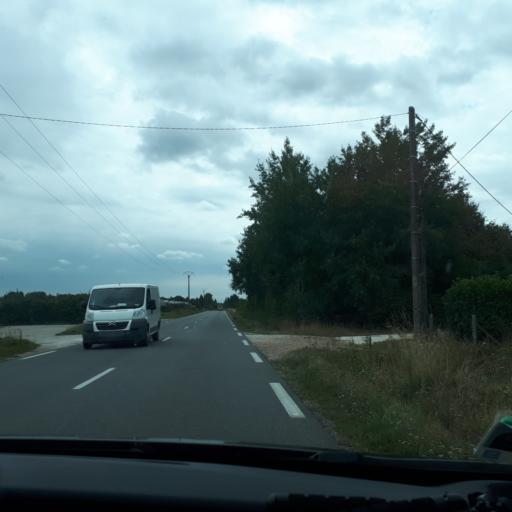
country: FR
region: Centre
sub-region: Departement du Loiret
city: Bray-en-Val
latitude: 47.8169
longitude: 2.3803
